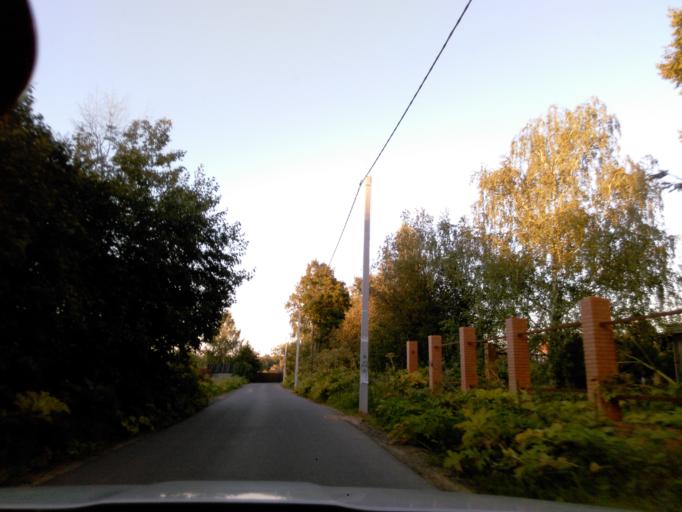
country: RU
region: Moskovskaya
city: Solnechnogorsk
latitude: 56.1300
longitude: 36.8513
